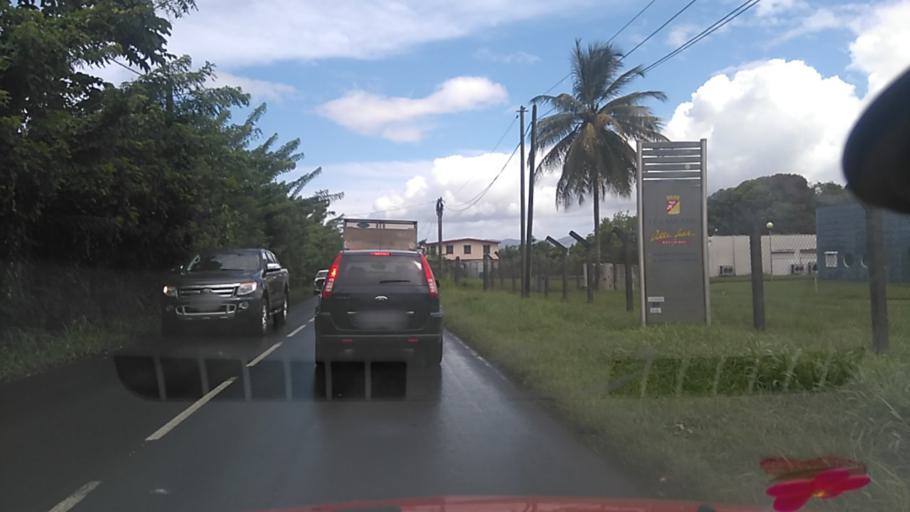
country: MQ
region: Martinique
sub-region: Martinique
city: Le Lamentin
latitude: 14.6256
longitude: -60.9894
